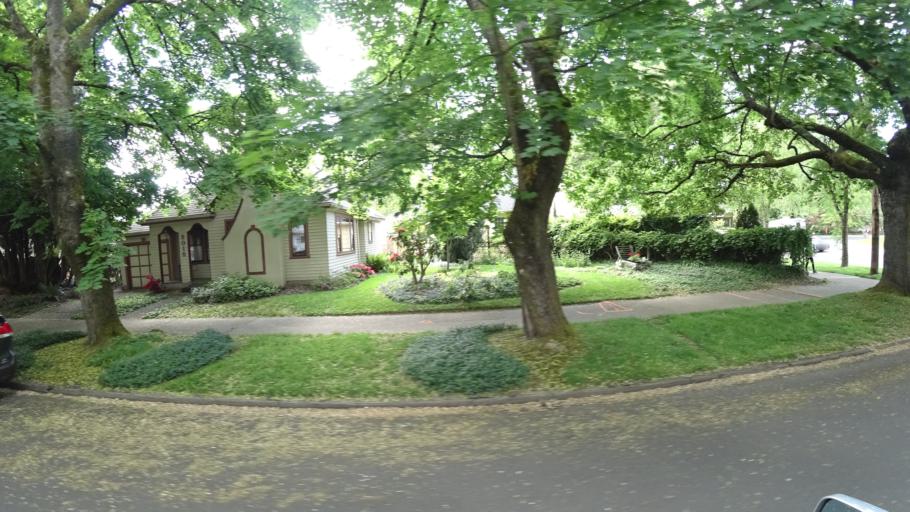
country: US
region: Oregon
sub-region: Multnomah County
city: Portland
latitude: 45.5079
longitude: -122.6494
